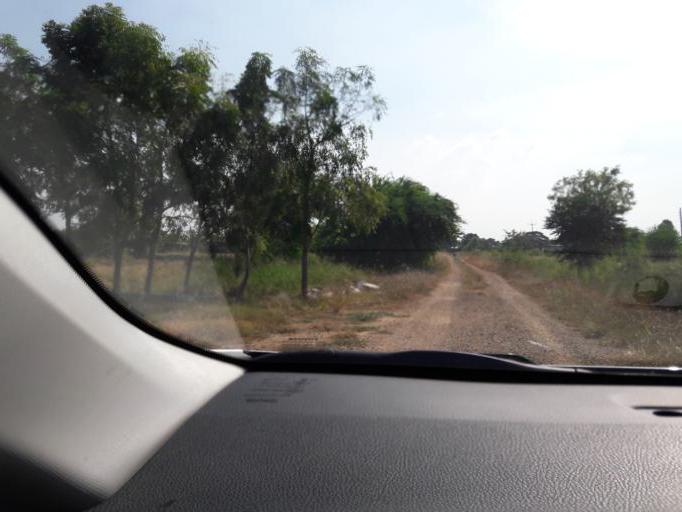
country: TH
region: Ang Thong
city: Wiset Chaichan
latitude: 14.5566
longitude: 100.3891
